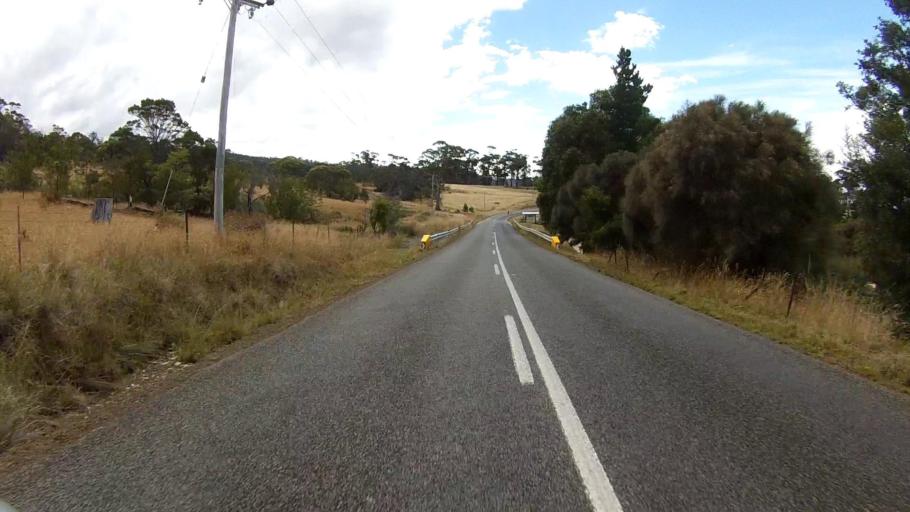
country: AU
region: Tasmania
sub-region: Sorell
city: Sorell
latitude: -42.2169
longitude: 148.0305
